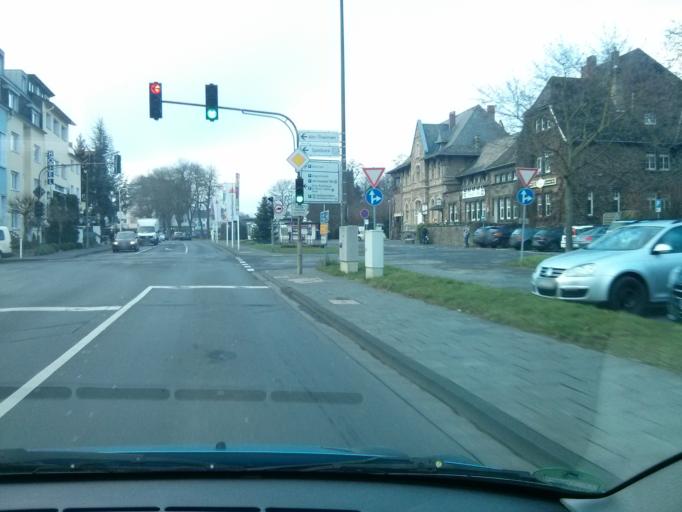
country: DE
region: Rheinland-Pfalz
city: Bad Neuenahr-Ahrweiler
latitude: 50.5471
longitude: 7.1452
